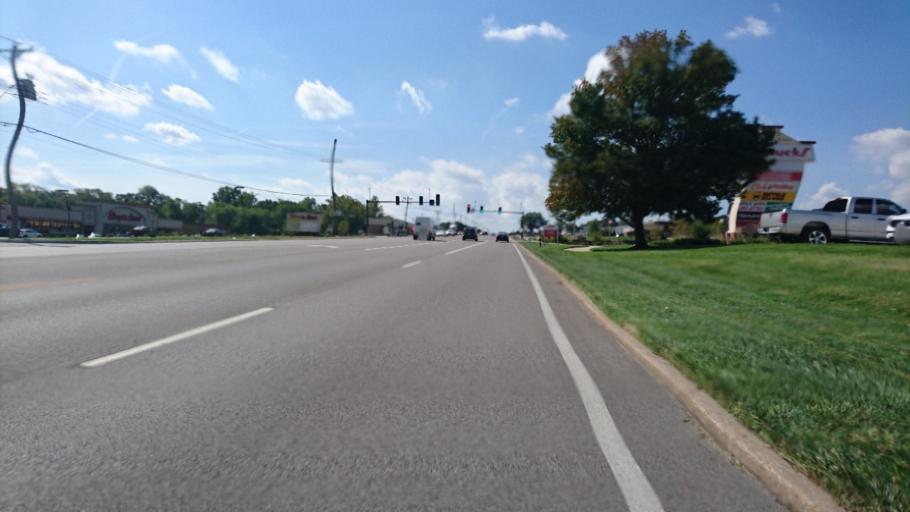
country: US
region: Missouri
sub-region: Saint Louis County
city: Ballwin
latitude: 38.5929
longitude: -90.5633
